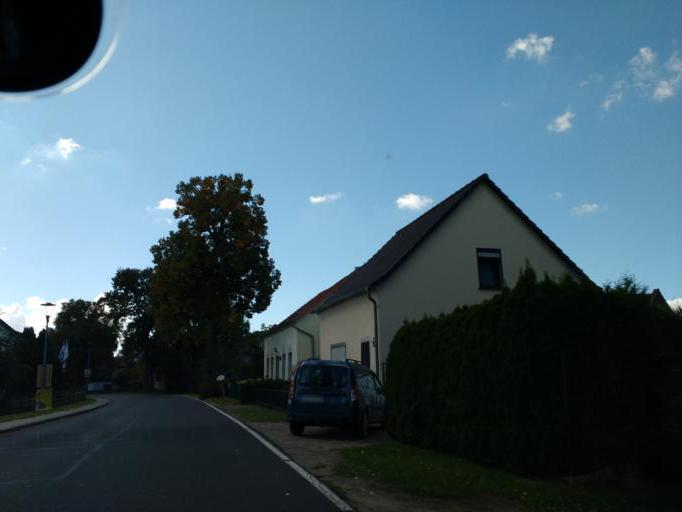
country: DE
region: Brandenburg
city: Mittenwalde
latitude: 52.2467
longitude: 13.5632
